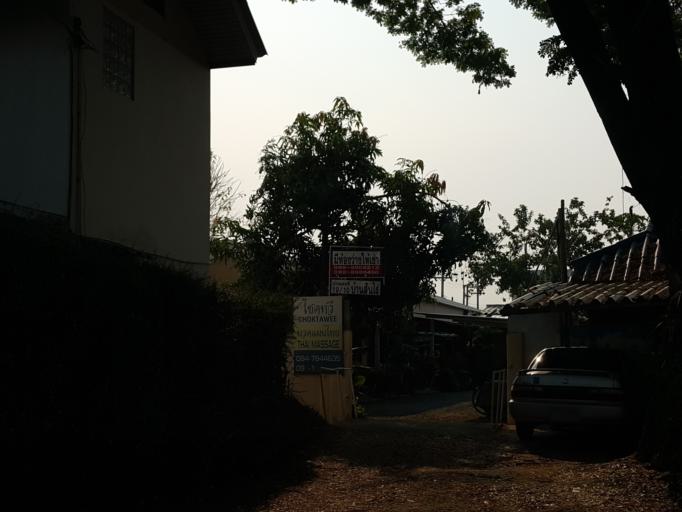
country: TH
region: Chiang Mai
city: San Kamphaeng
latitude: 18.7505
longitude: 99.1061
